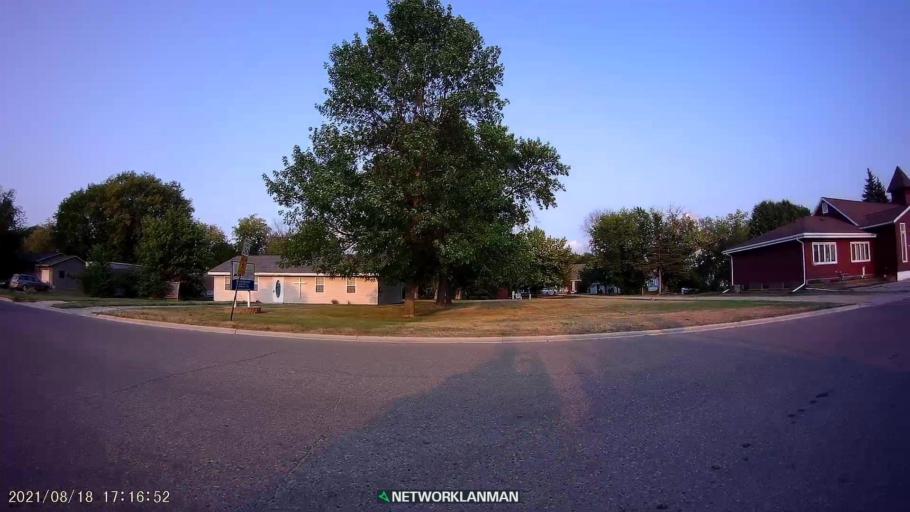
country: US
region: Minnesota
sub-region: Roseau County
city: Warroad
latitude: 48.9050
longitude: -95.3137
